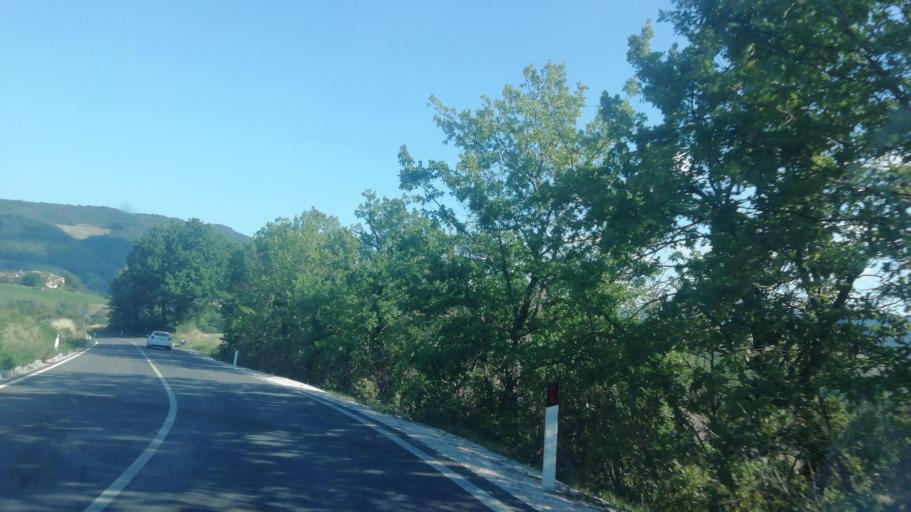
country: IT
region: The Marches
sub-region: Provincia di Pesaro e Urbino
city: Frontone
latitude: 43.5380
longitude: 12.7418
